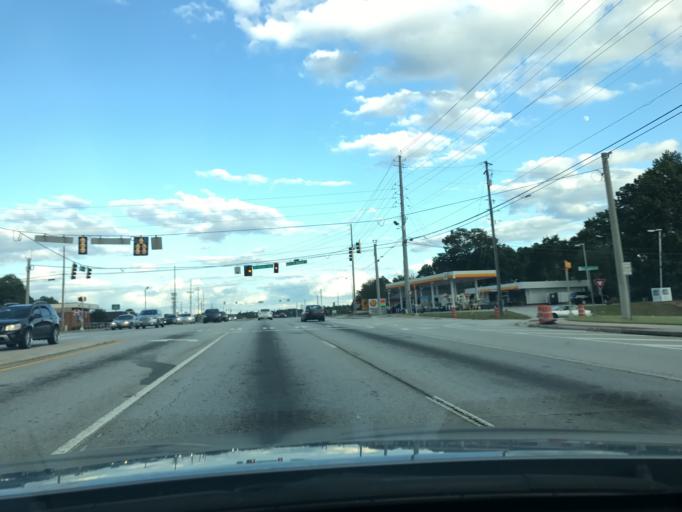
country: US
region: Georgia
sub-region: Douglas County
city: Douglasville
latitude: 33.7511
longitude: -84.7213
